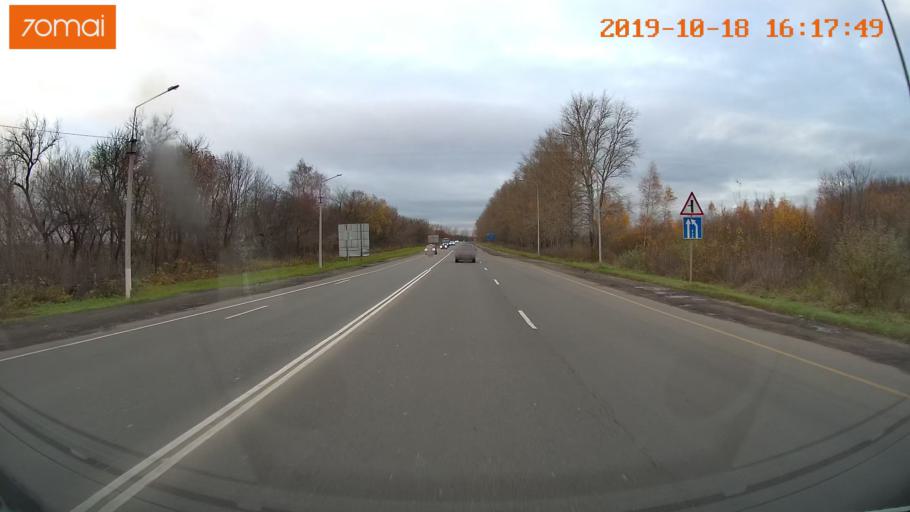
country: RU
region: Vladimir
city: Kommunar
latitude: 56.1789
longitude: 40.4534
